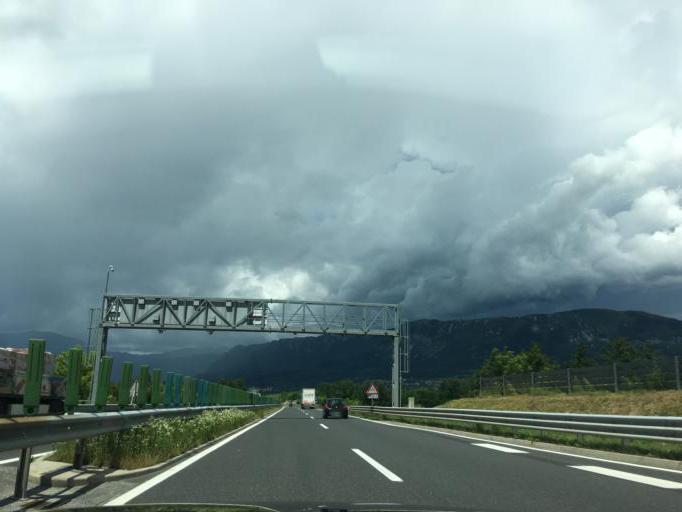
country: SI
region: Vipava
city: Vipava
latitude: 45.8393
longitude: 13.9530
